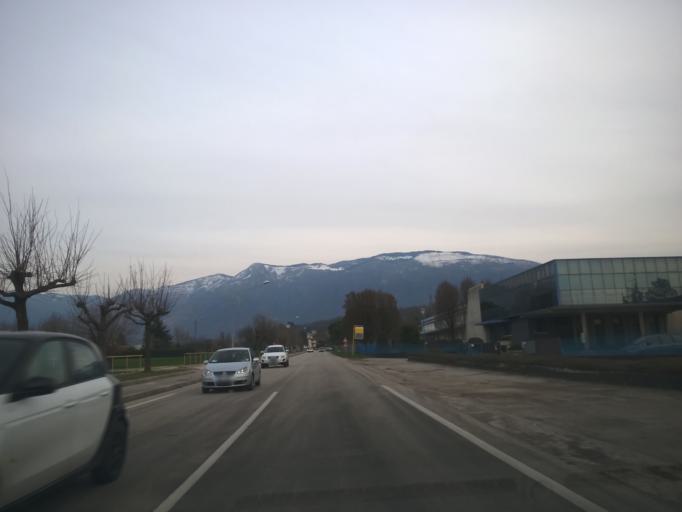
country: IT
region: Veneto
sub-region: Provincia di Vicenza
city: Carre
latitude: 45.7352
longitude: 11.4645
